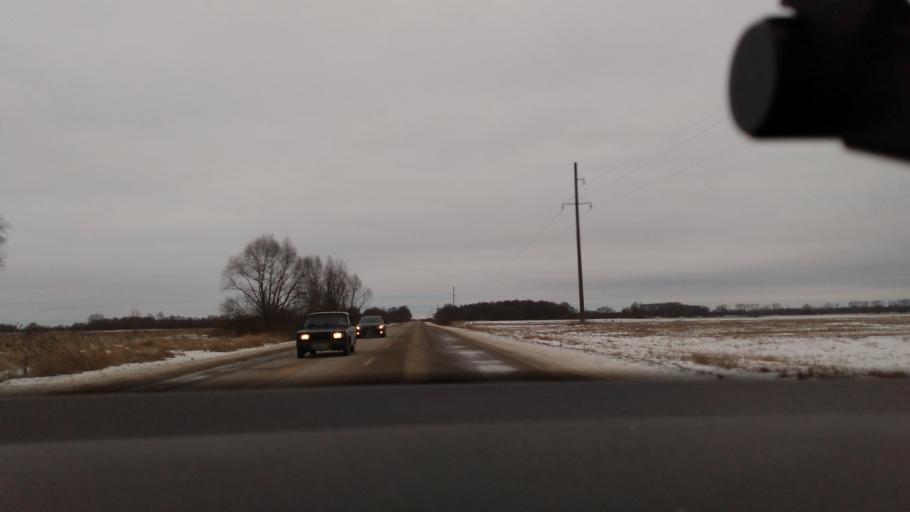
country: RU
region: Moskovskaya
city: Krasnaya Poyma
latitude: 55.1044
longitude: 39.1473
